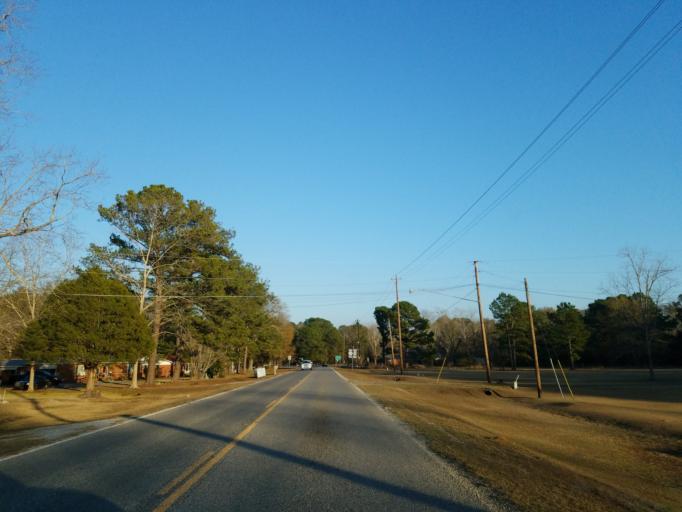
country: US
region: Mississippi
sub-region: Clarke County
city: Stonewall
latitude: 32.1704
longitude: -88.8353
